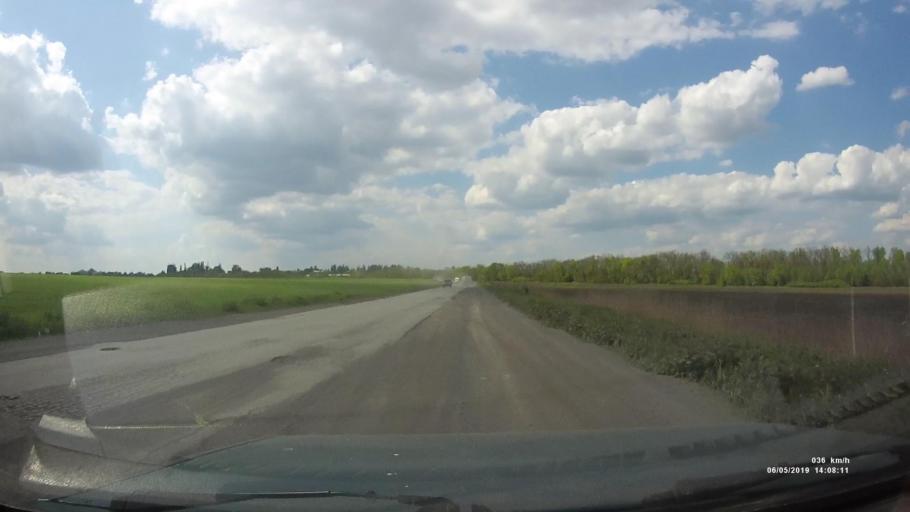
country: RU
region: Rostov
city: Shakhty
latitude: 47.6823
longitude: 40.2998
